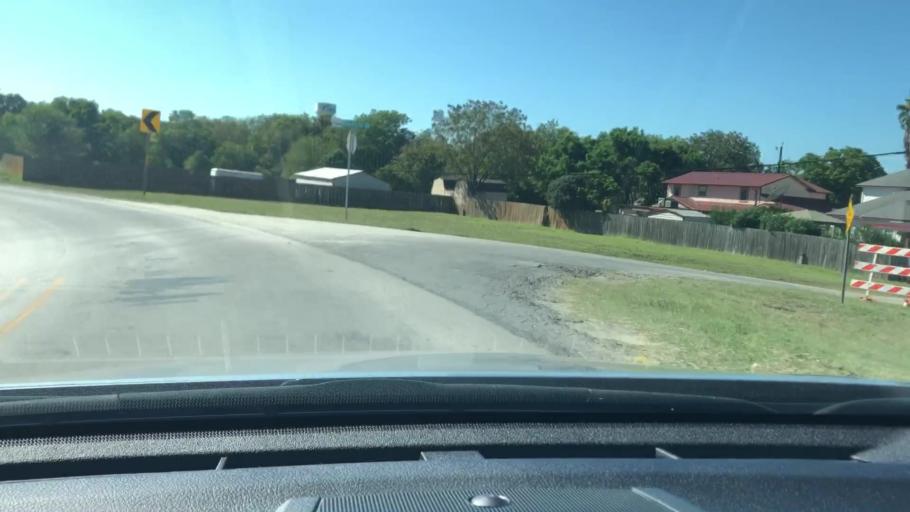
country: US
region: Texas
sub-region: Bexar County
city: Selma
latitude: 29.5786
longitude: -98.3223
